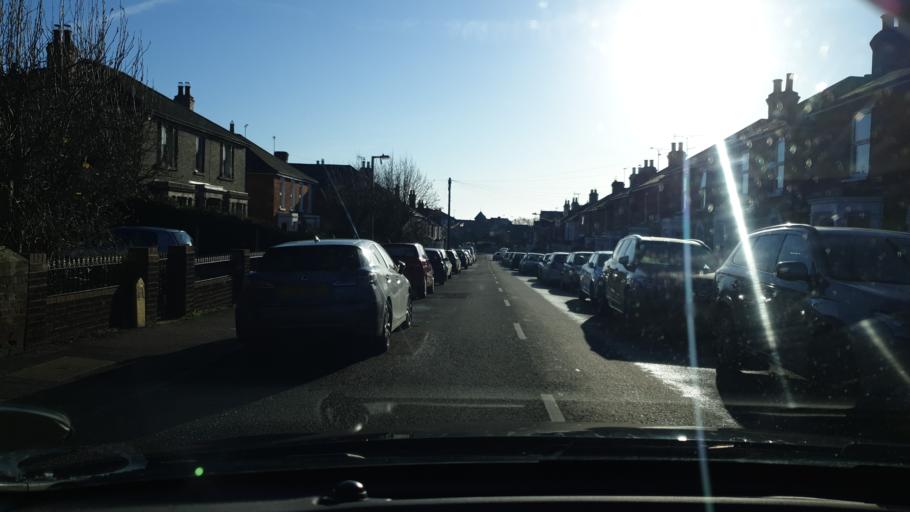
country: GB
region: England
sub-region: Essex
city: Brightlingsea
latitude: 51.8131
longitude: 1.0232
